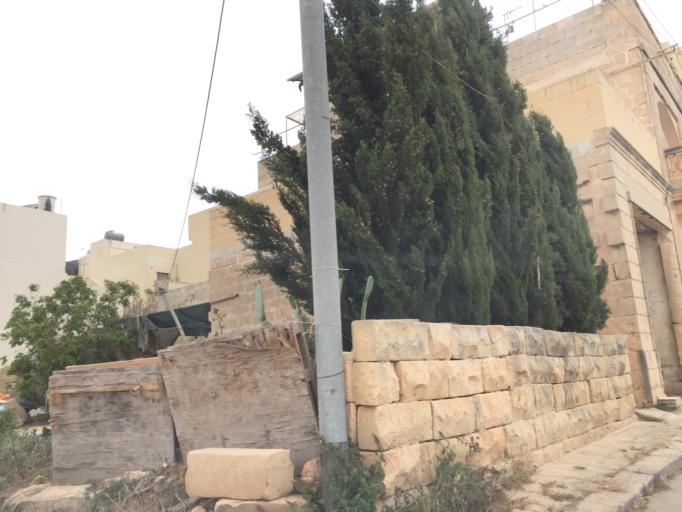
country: MT
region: L-Imgarr
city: Imgarr
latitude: 35.9188
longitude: 14.3687
